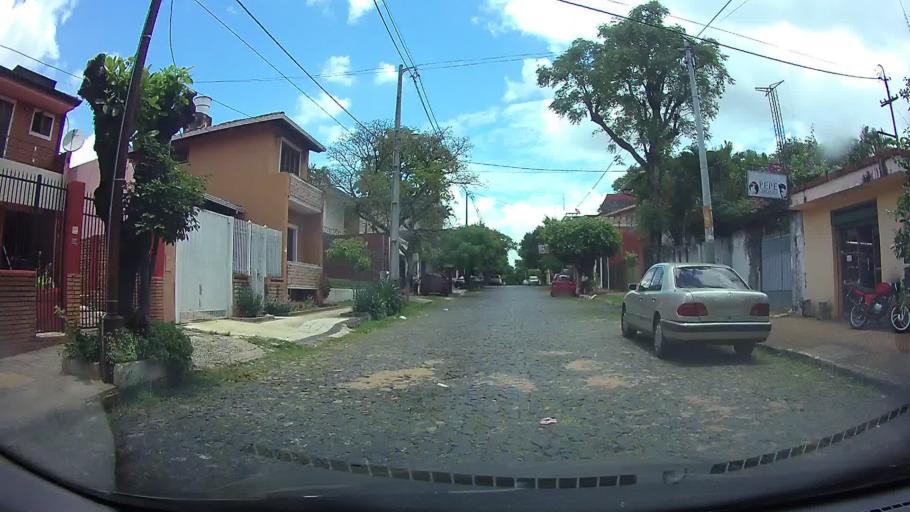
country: PY
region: Central
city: Lambare
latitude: -25.3124
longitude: -57.5939
